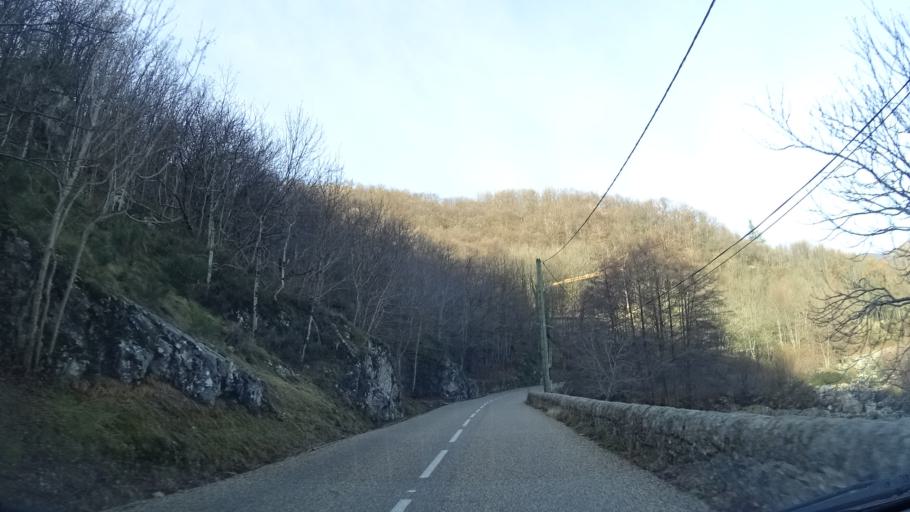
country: FR
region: Rhone-Alpes
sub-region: Departement de l'Ardeche
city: Thueyts
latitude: 44.7247
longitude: 4.2611
